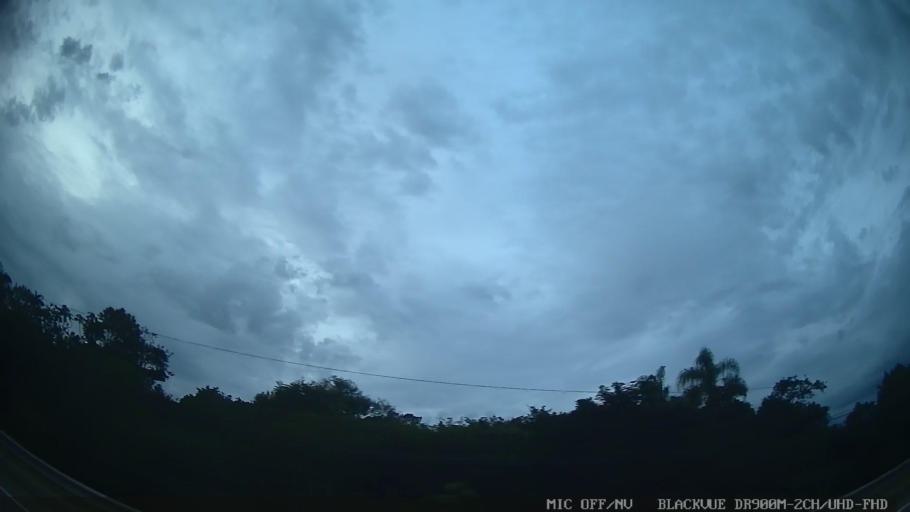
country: BR
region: Sao Paulo
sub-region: Amparo
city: Amparo
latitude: -22.8420
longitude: -46.7744
